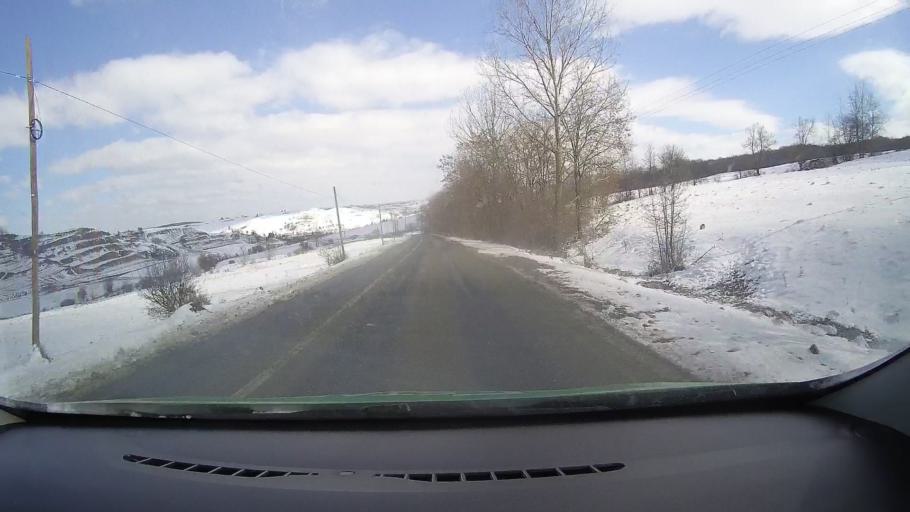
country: RO
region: Sibiu
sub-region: Comuna Barghis
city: Barghis
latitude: 45.9792
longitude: 24.5191
